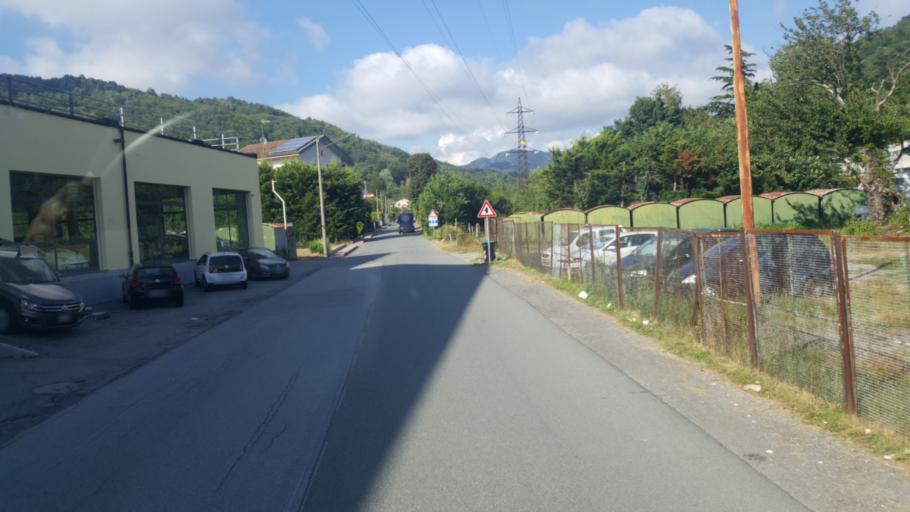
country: IT
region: Liguria
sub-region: Provincia di Genova
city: Busalla
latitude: 44.5729
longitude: 8.9597
